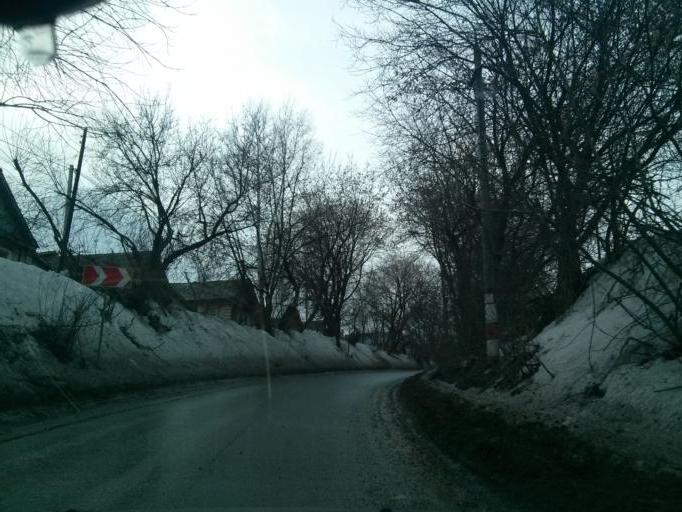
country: RU
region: Nizjnij Novgorod
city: Afonino
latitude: 56.2940
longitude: 44.0948
